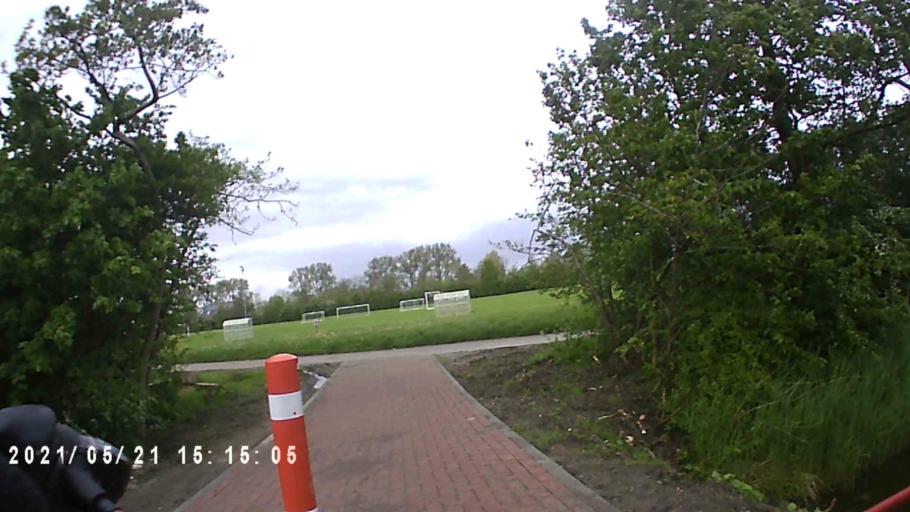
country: NL
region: Groningen
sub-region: Gemeente Zuidhorn
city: Aduard
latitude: 53.2583
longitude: 6.4560
